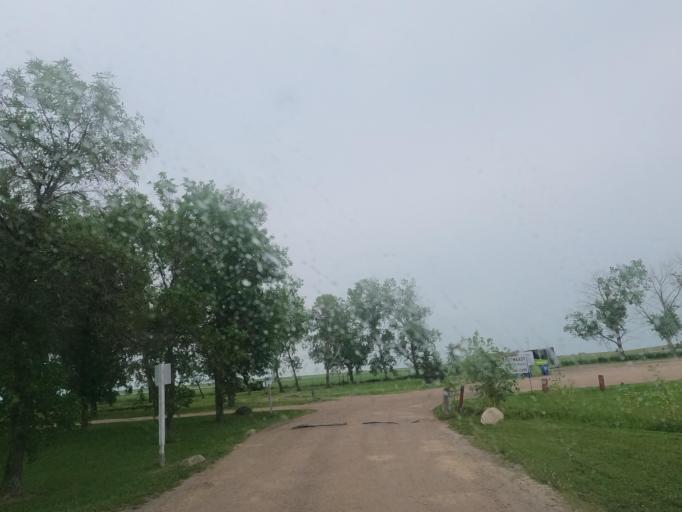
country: CA
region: Manitoba
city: Winnipeg
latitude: 49.8274
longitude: -96.9774
